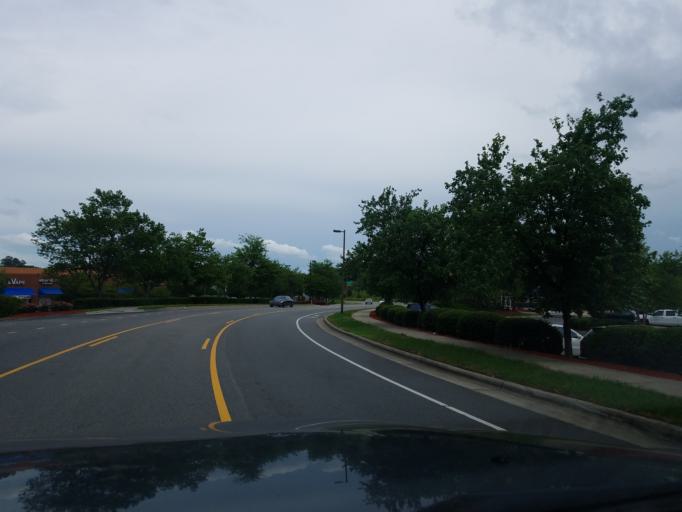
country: US
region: North Carolina
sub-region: Durham County
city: Durham
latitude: 36.0302
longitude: -78.9222
